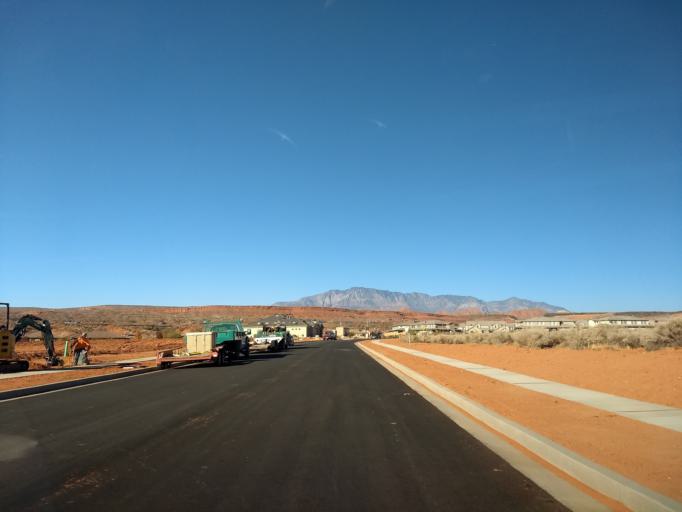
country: US
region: Utah
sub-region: Washington County
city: Washington
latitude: 37.1421
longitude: -113.4792
